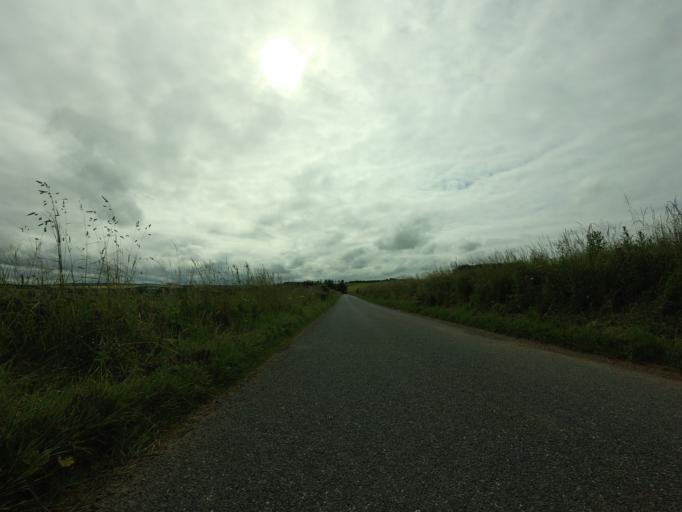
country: GB
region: Scotland
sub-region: Aberdeenshire
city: Turriff
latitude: 57.5328
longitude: -2.3976
